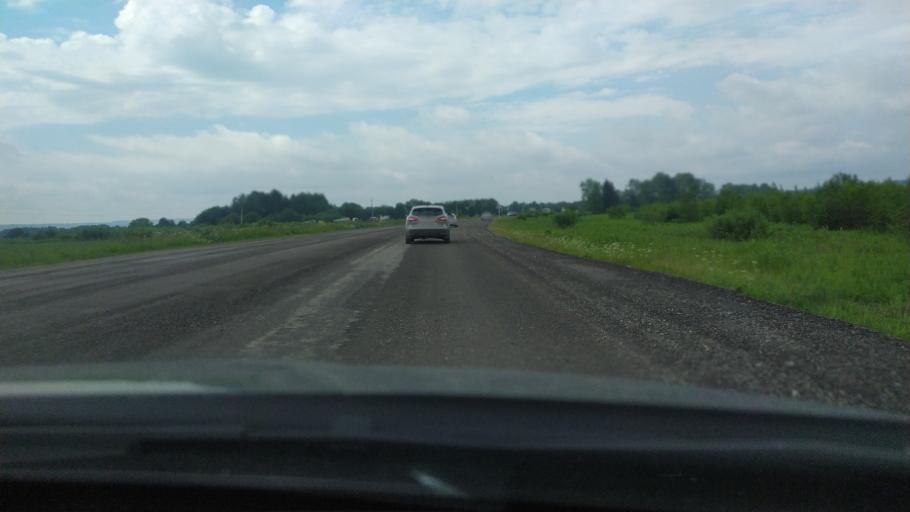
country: RU
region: Perm
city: Kalino
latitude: 58.2901
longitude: 57.4645
